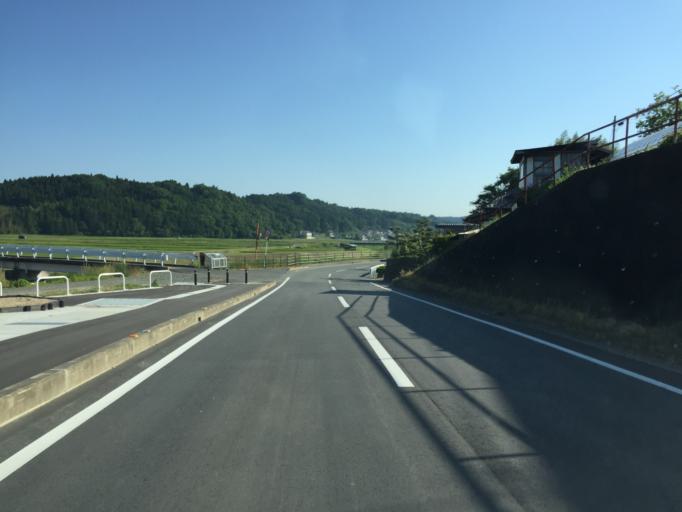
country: JP
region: Ibaraki
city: Kitaibaraki
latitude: 36.8892
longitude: 140.7541
